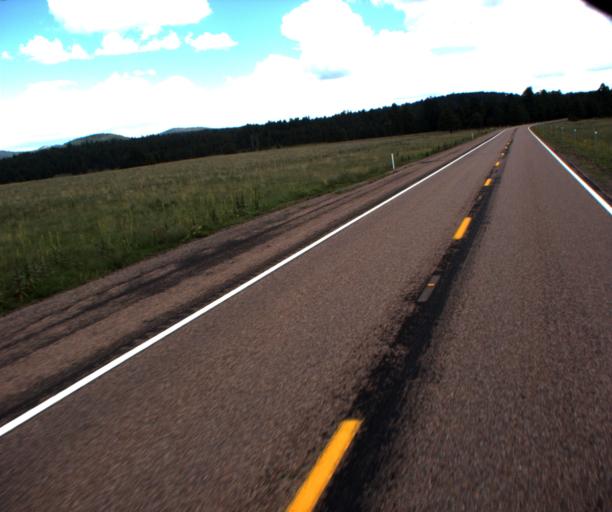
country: US
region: Arizona
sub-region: Navajo County
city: Pinetop-Lakeside
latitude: 34.0426
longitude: -109.6818
